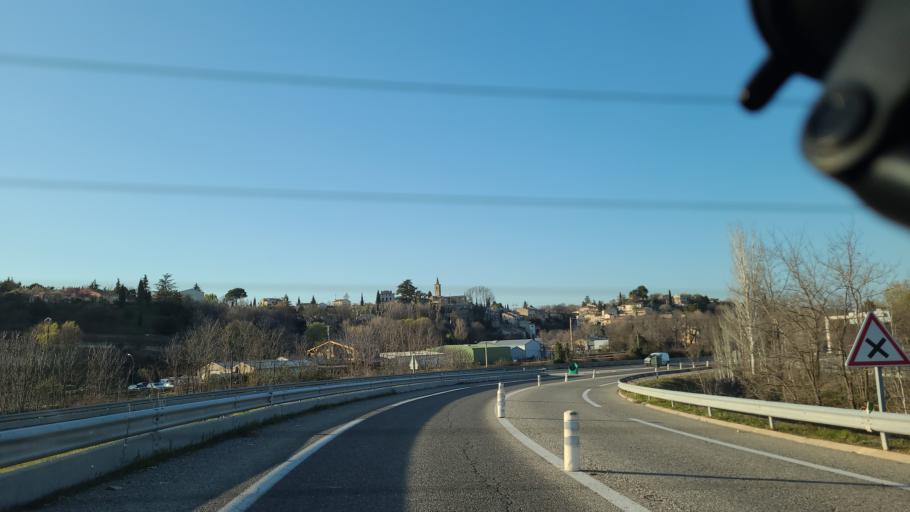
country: FR
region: Provence-Alpes-Cote d'Azur
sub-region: Departement des Alpes-de-Haute-Provence
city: Oraison
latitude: 43.9215
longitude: 5.8923
